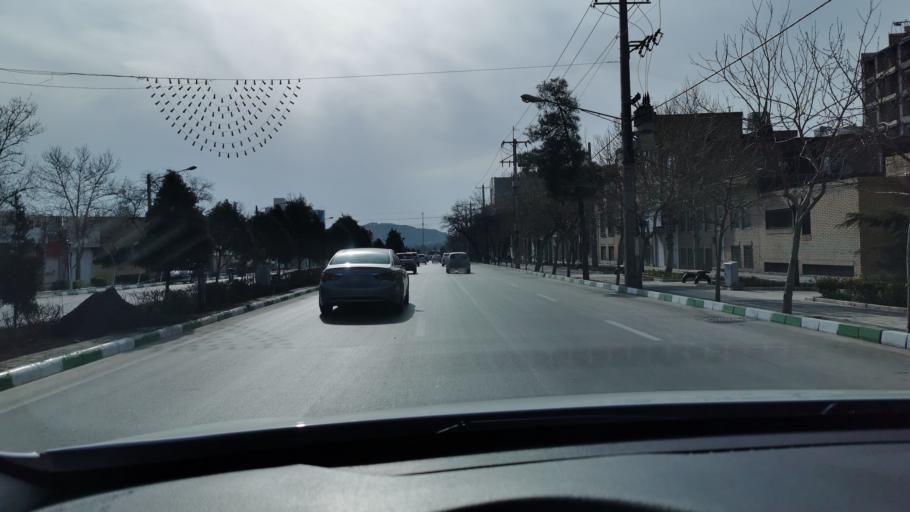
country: IR
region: Razavi Khorasan
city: Mashhad
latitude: 36.2863
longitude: 59.5456
